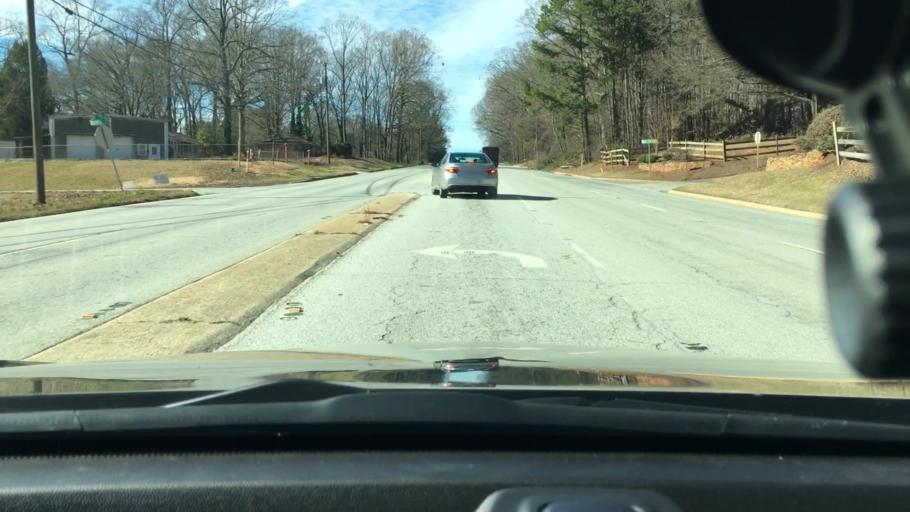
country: US
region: South Carolina
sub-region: Spartanburg County
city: Spartanburg
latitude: 34.9271
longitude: -81.8539
